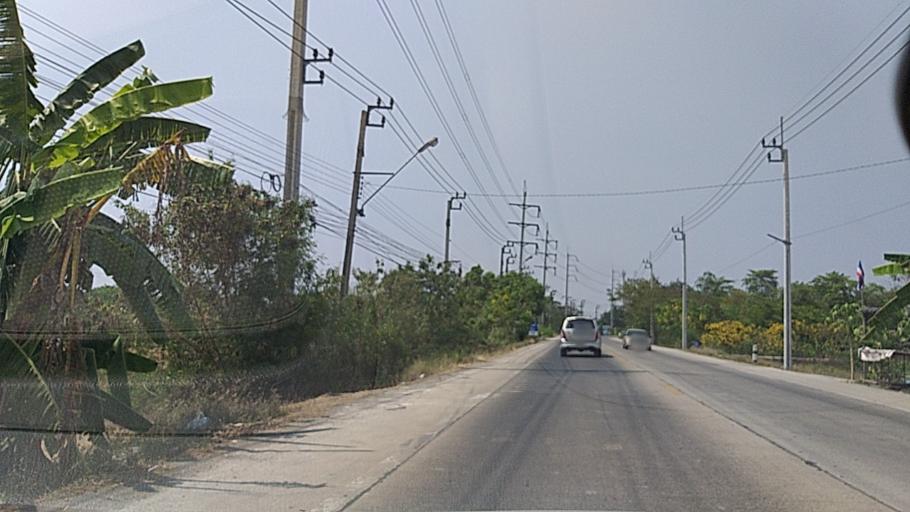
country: TH
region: Nonthaburi
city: Sai Noi
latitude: 13.9537
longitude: 100.3117
